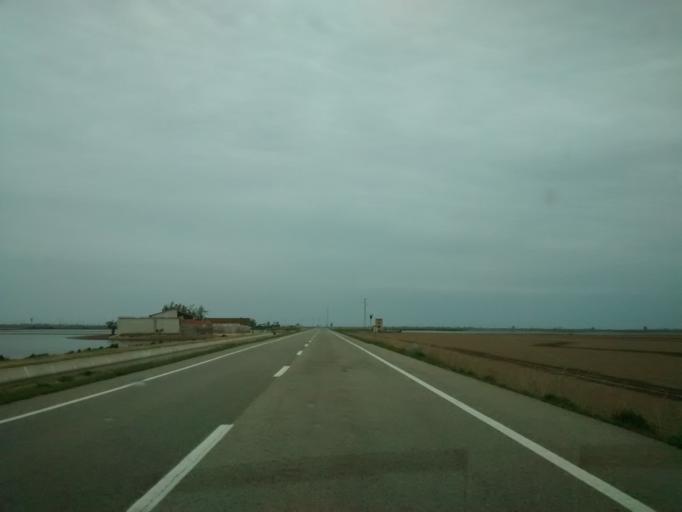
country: ES
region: Catalonia
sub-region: Provincia de Tarragona
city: Deltebre
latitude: 40.6972
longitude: 0.6791
